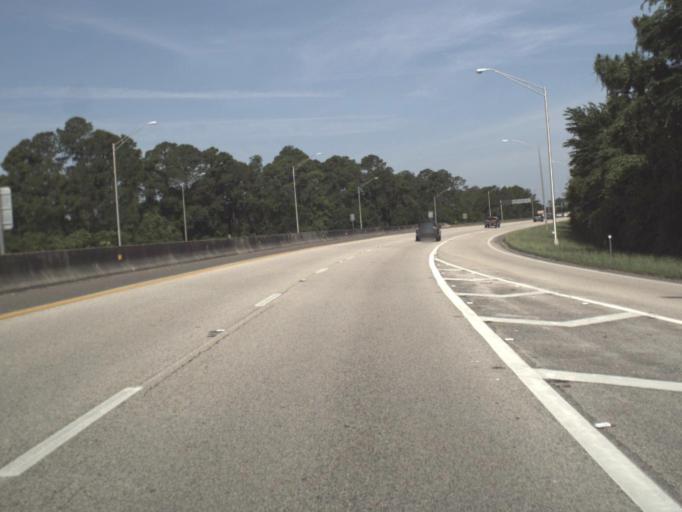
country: US
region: Florida
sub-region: Saint Johns County
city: Ponte Vedra Beach
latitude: 30.2564
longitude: -81.4010
